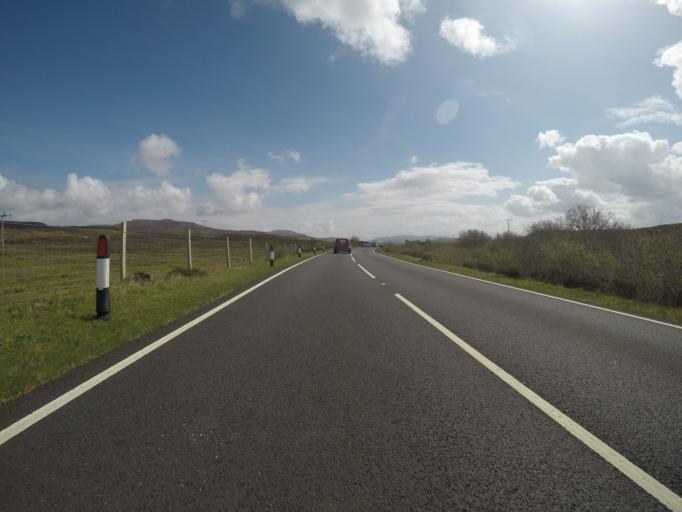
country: GB
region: Scotland
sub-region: Highland
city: Portree
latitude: 57.5046
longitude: -6.3320
